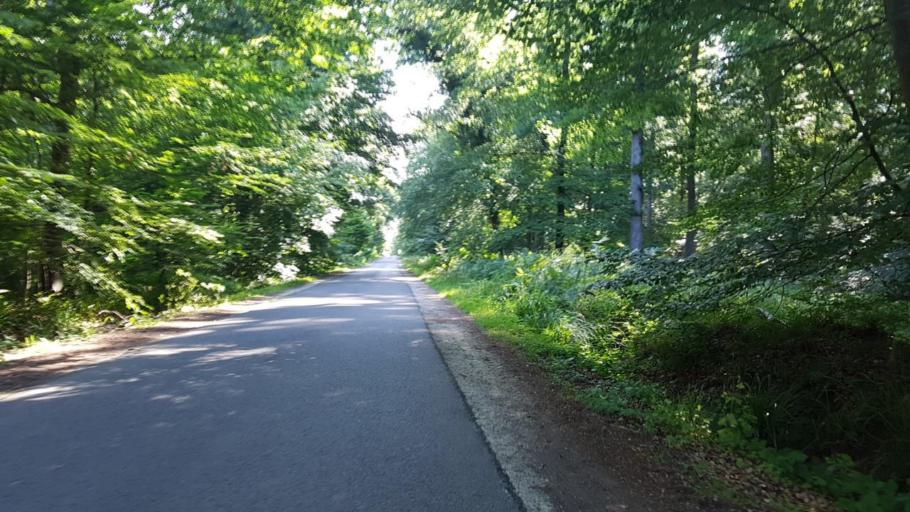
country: FR
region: Picardie
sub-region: Departement de l'Oise
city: Pontpoint
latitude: 49.2876
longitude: 2.6280
